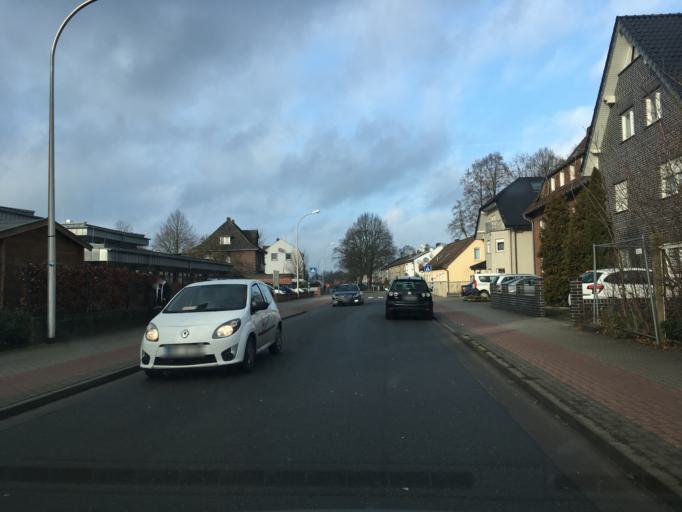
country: DE
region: North Rhine-Westphalia
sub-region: Regierungsbezirk Munster
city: Gronau
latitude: 52.2178
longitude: 7.0192
